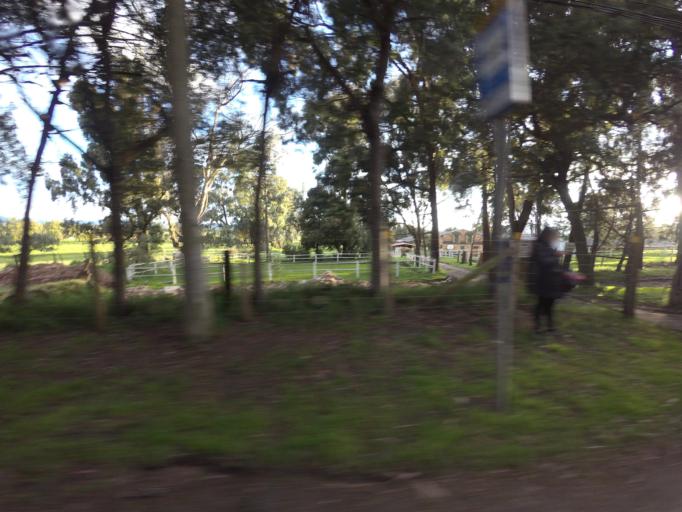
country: CO
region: Cundinamarca
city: Cota
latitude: 4.7940
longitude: -74.0305
